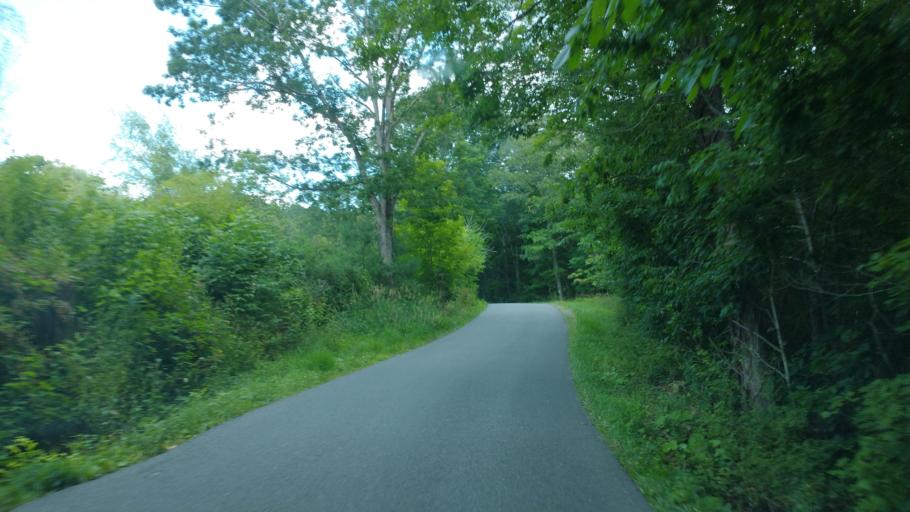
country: US
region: West Virginia
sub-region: Mercer County
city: Athens
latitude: 37.4605
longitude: -81.0502
